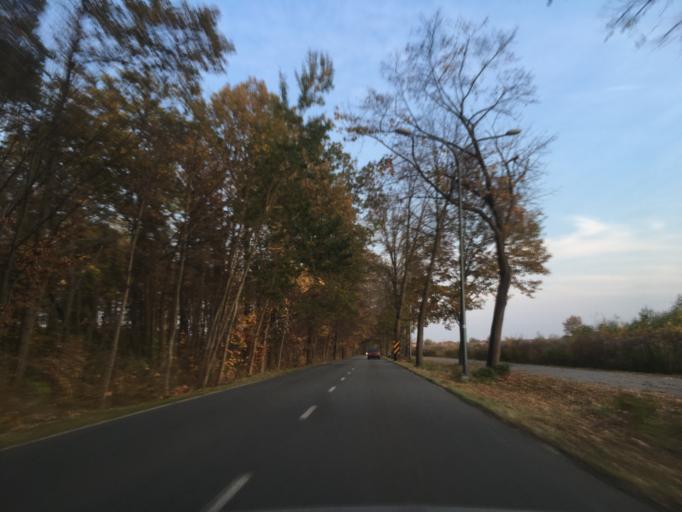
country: PL
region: Masovian Voivodeship
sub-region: Powiat pruszkowski
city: Nadarzyn
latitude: 52.0912
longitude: 20.8478
